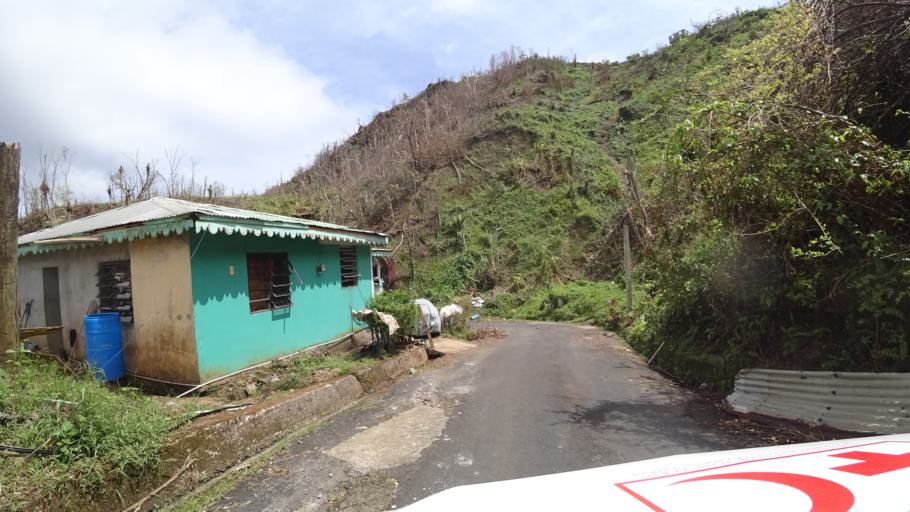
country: DM
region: Saint David
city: Rosalie
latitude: 15.3954
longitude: -61.2587
